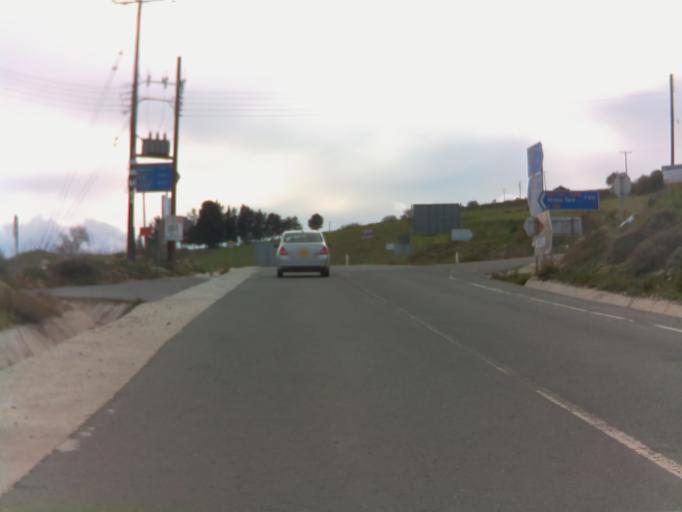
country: CY
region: Pafos
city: Polis
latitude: 34.9593
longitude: 32.4131
